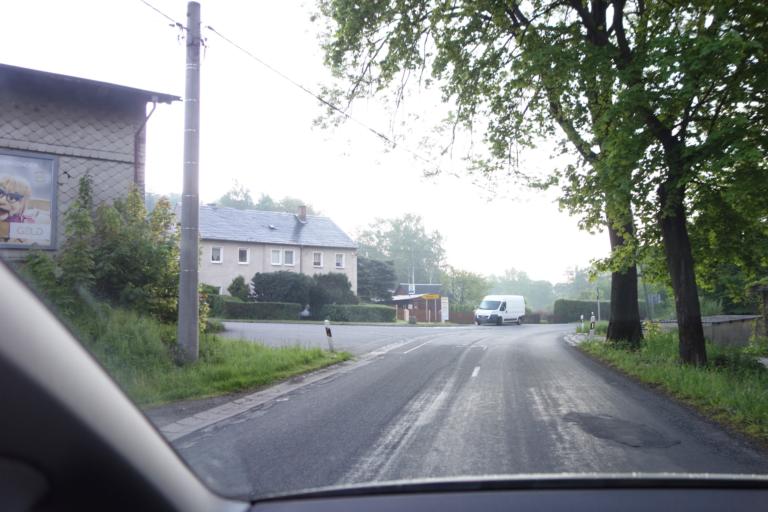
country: DE
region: Saxony
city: Pockau
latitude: 50.6905
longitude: 13.2534
